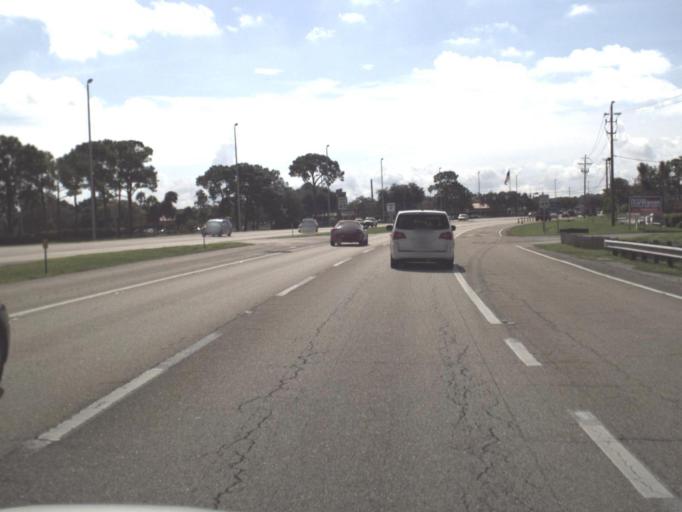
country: US
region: Florida
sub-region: Sarasota County
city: Vamo
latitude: 27.2324
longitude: -82.4968
